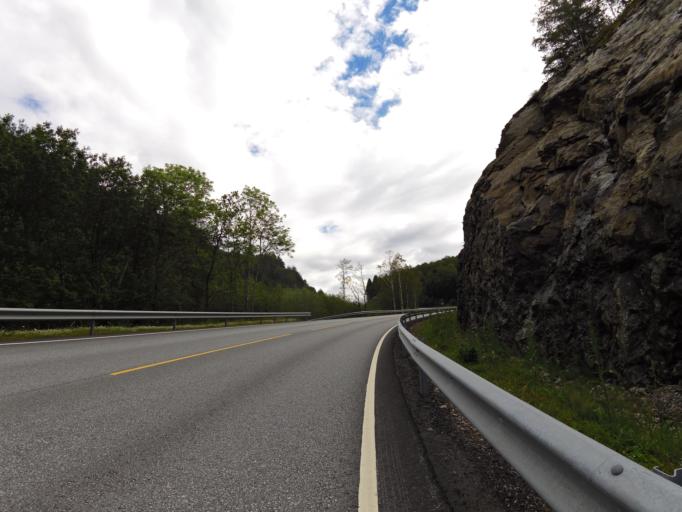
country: NO
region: Vest-Agder
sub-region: Lindesnes
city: Vigeland
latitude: 58.0527
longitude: 7.2074
